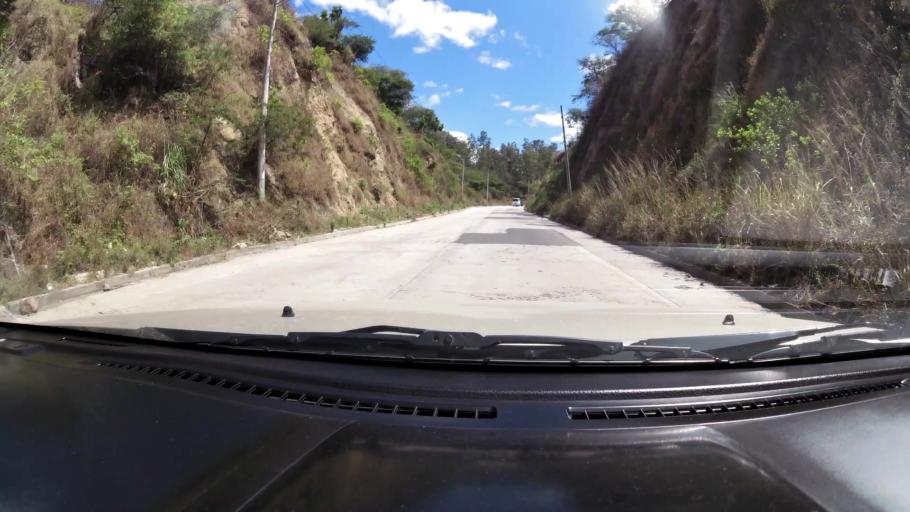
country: EC
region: Azuay
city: Cuenca
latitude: -3.2201
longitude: -79.2034
